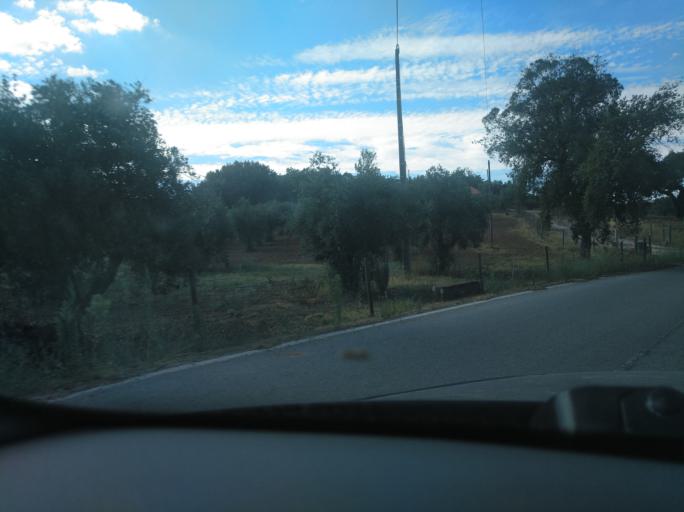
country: ES
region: Extremadura
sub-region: Provincia de Badajoz
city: La Codosera
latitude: 39.1755
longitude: -7.1794
